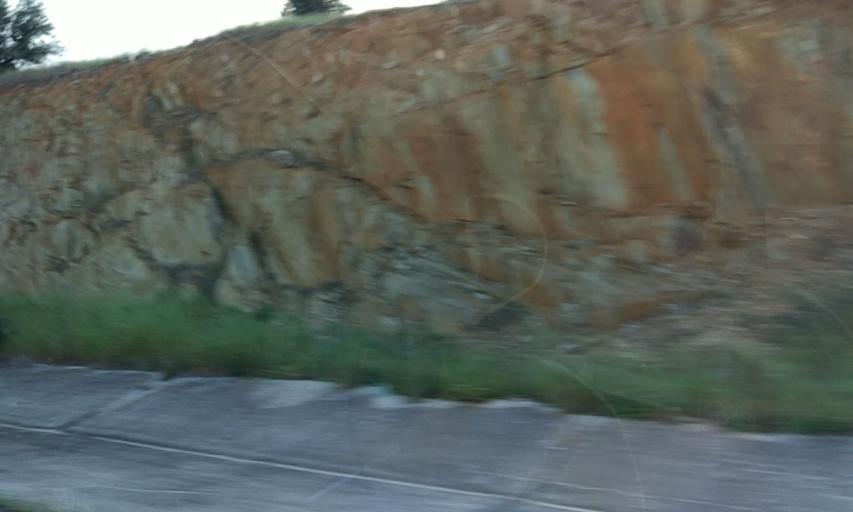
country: ES
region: Extremadura
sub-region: Provincia de Caceres
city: Santiago del Campo
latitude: 39.6359
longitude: -6.3934
